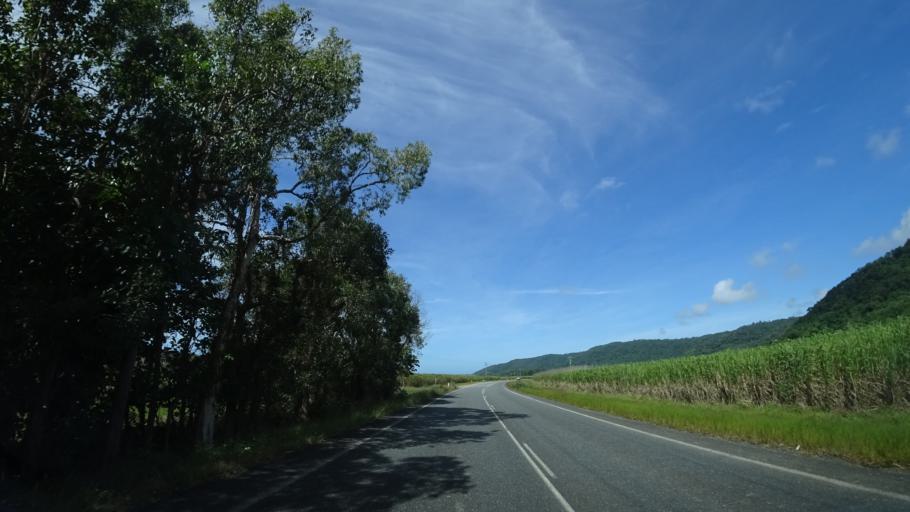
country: AU
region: Queensland
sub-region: Cairns
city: Port Douglas
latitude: -16.2921
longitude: 145.3873
